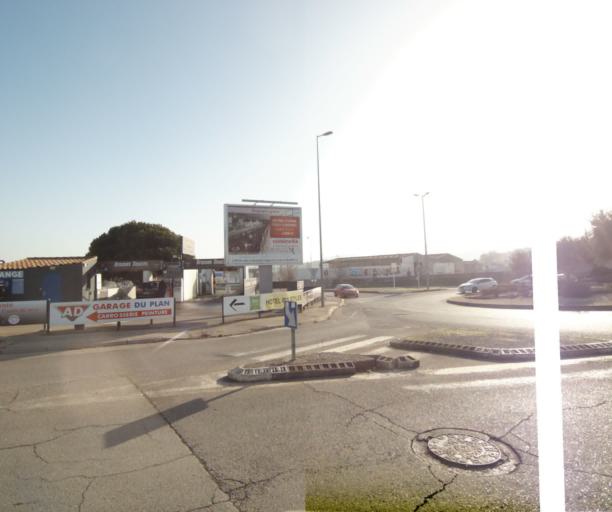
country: FR
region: Provence-Alpes-Cote d'Azur
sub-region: Departement des Bouches-du-Rhone
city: Septemes-les-Vallons
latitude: 43.4154
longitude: 5.3514
